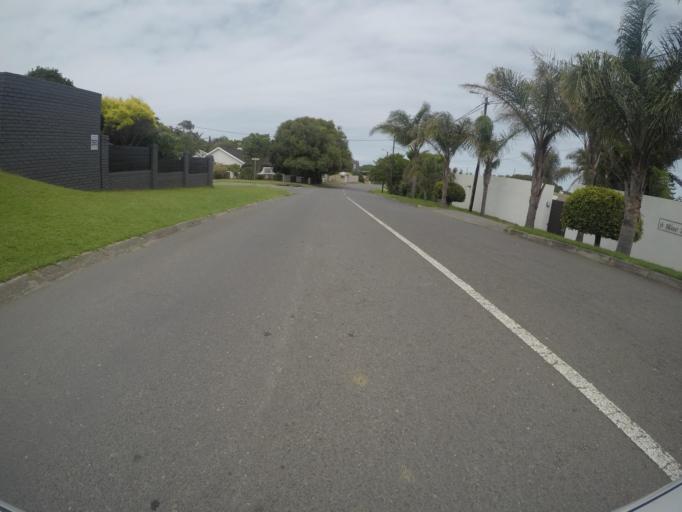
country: ZA
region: Eastern Cape
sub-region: Buffalo City Metropolitan Municipality
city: East London
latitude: -32.9804
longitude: 27.9491
